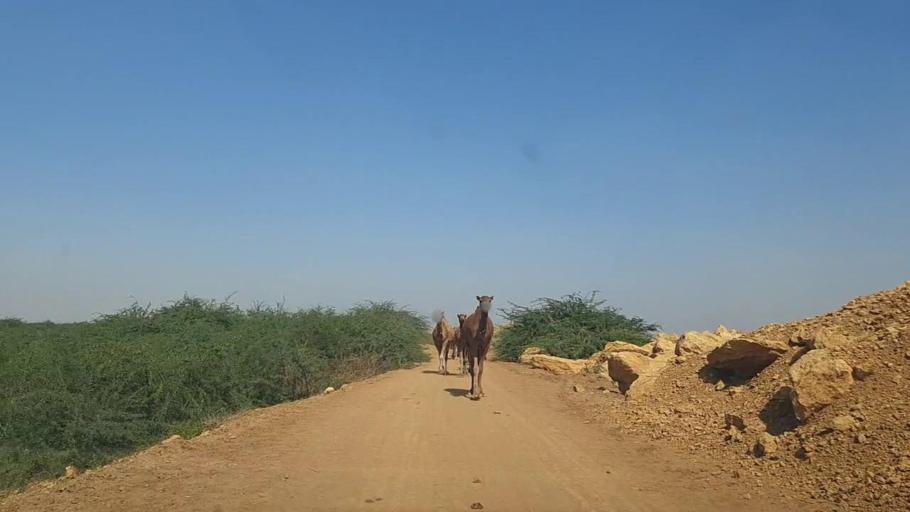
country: PK
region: Sindh
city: Thatta
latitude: 24.8321
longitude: 68.0191
